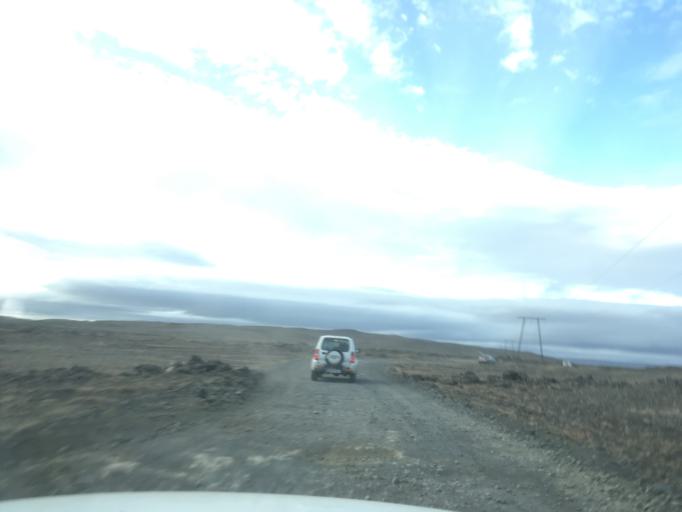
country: IS
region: South
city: Vestmannaeyjar
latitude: 64.1442
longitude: -19.1314
